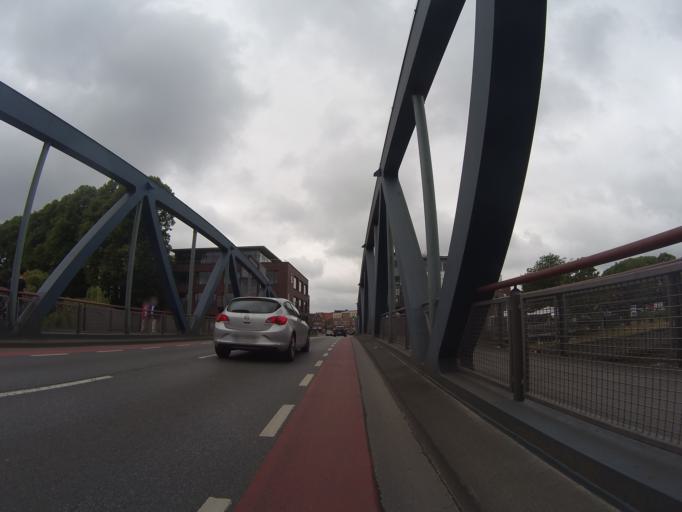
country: DE
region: Lower Saxony
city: Meppen
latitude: 52.6943
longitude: 7.2927
